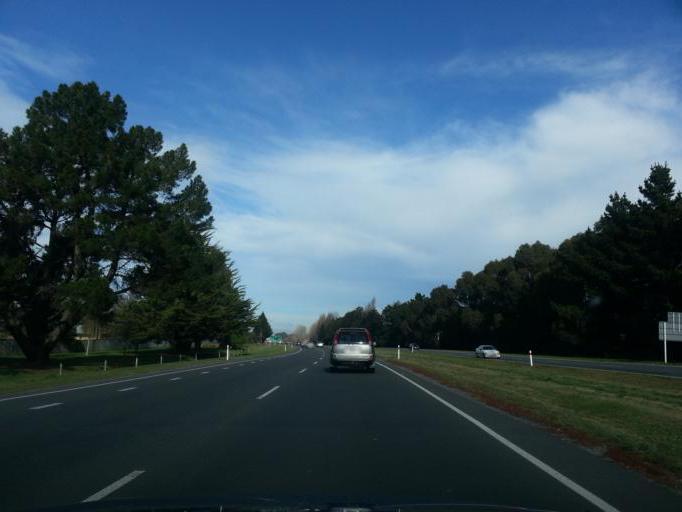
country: NZ
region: Canterbury
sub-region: Waimakariri District
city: Kaiapoi
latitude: -43.3912
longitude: 172.6400
